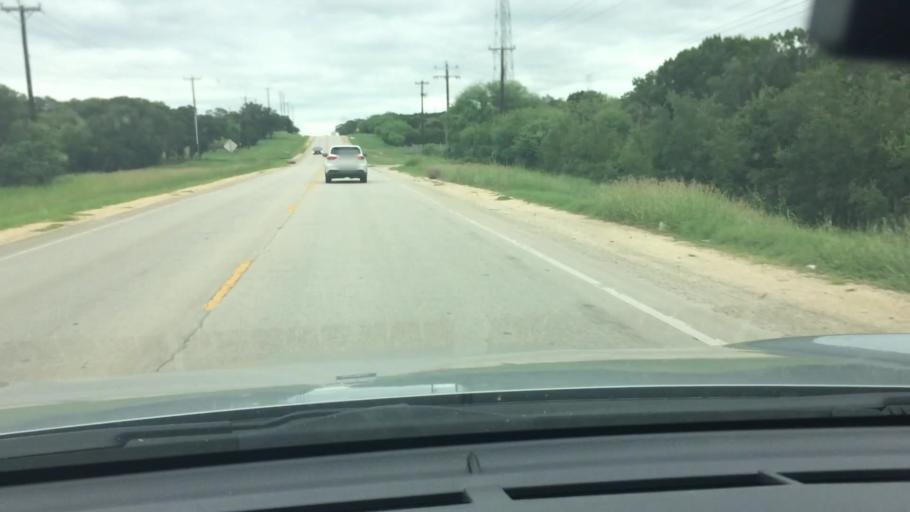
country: US
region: Texas
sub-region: Comal County
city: Garden Ridge
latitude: 29.6436
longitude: -98.3940
